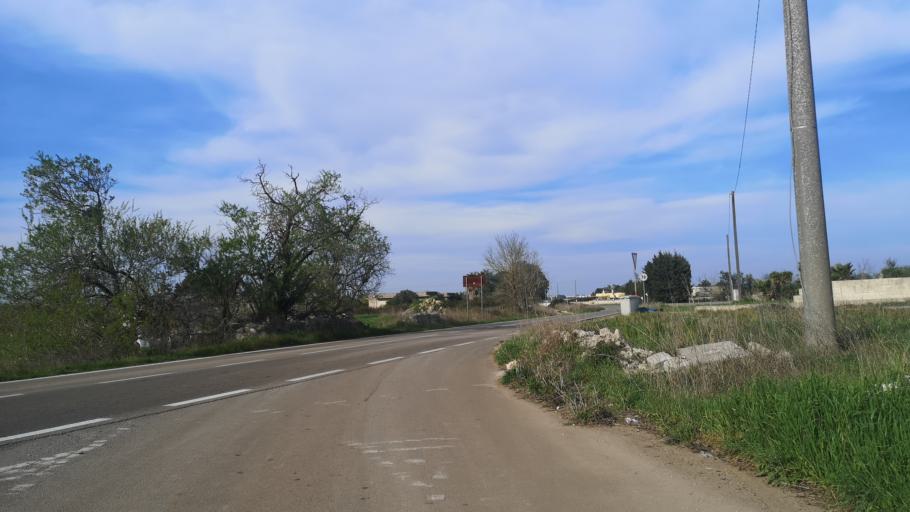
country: IT
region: Apulia
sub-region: Provincia di Lecce
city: Spongano
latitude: 40.0232
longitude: 18.3705
